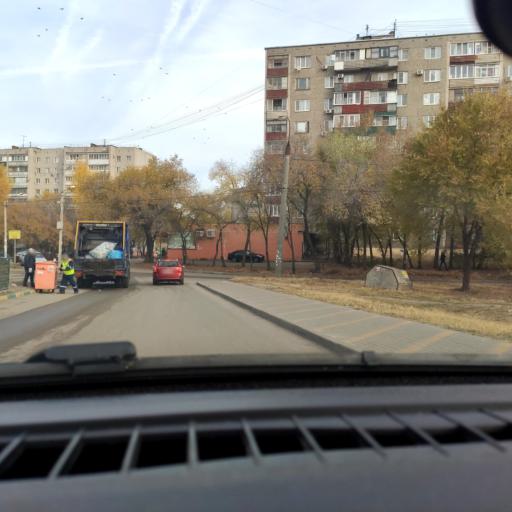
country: RU
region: Voronezj
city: Voronezh
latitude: 51.7186
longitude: 39.2656
